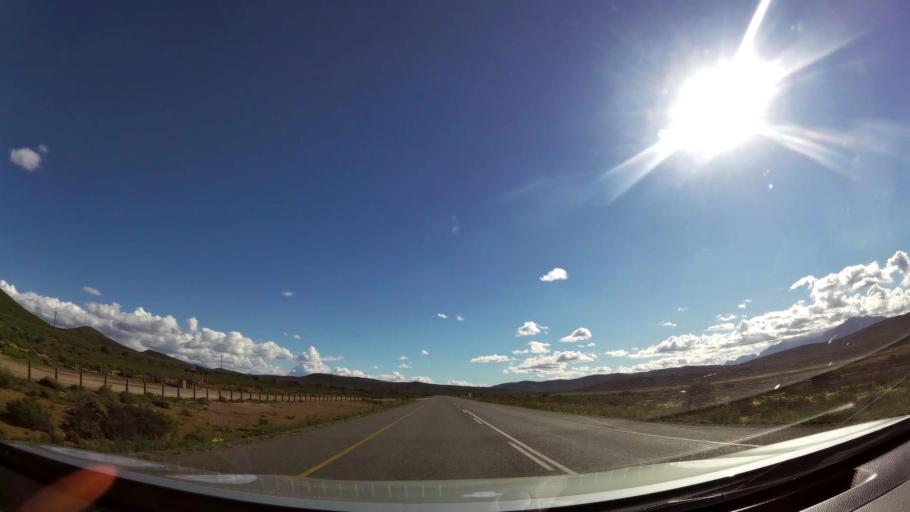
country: ZA
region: Western Cape
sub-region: Cape Winelands District Municipality
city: Worcester
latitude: -33.7521
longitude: 19.7226
